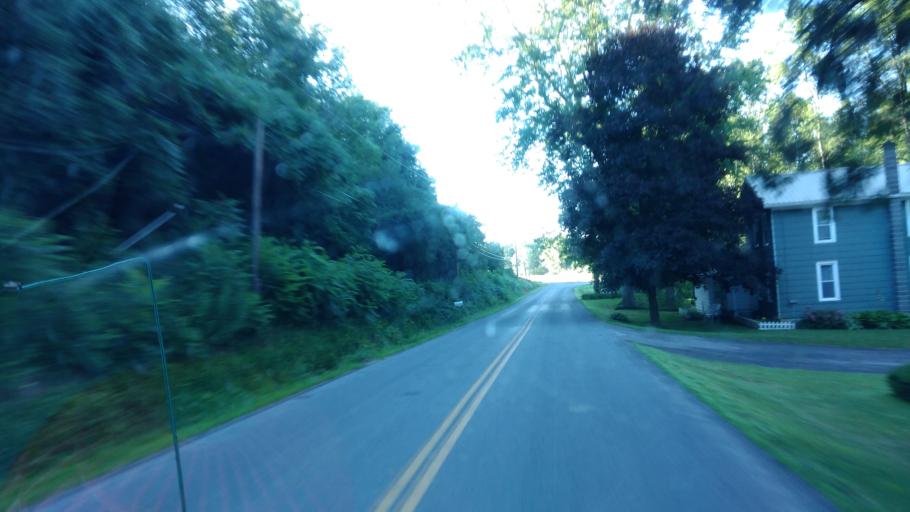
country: US
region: New York
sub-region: Wayne County
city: Lyons
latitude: 43.0804
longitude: -77.0162
